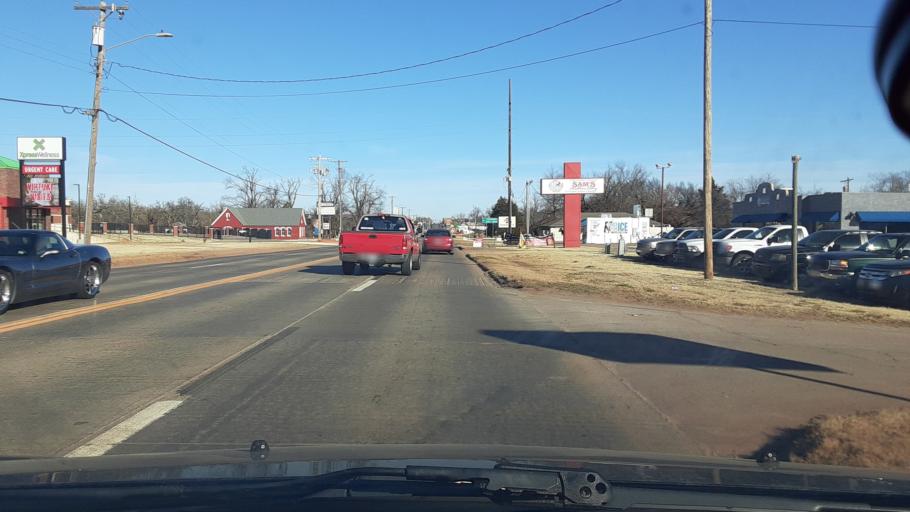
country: US
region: Oklahoma
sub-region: Logan County
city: Guthrie
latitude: 35.8659
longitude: -97.4253
